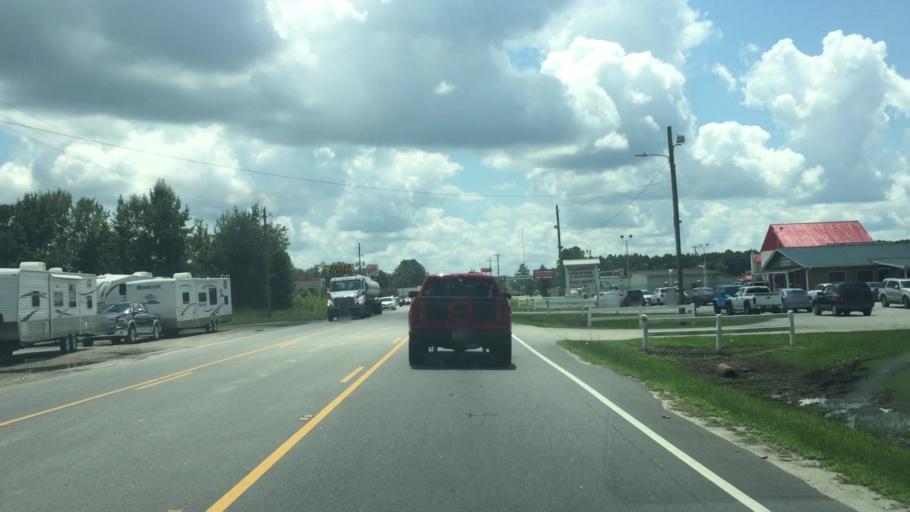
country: US
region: North Carolina
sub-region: Columbus County
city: Chadbourn
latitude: 34.3347
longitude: -78.8269
